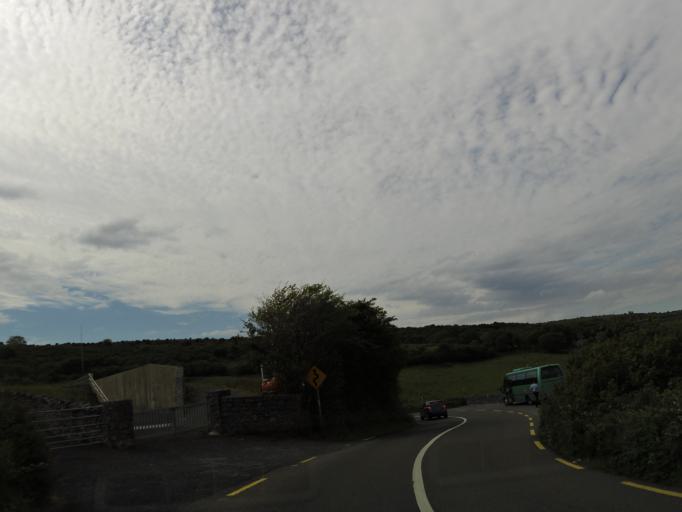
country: IE
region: Connaught
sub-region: County Galway
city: Bearna
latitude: 53.0701
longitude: -9.1887
